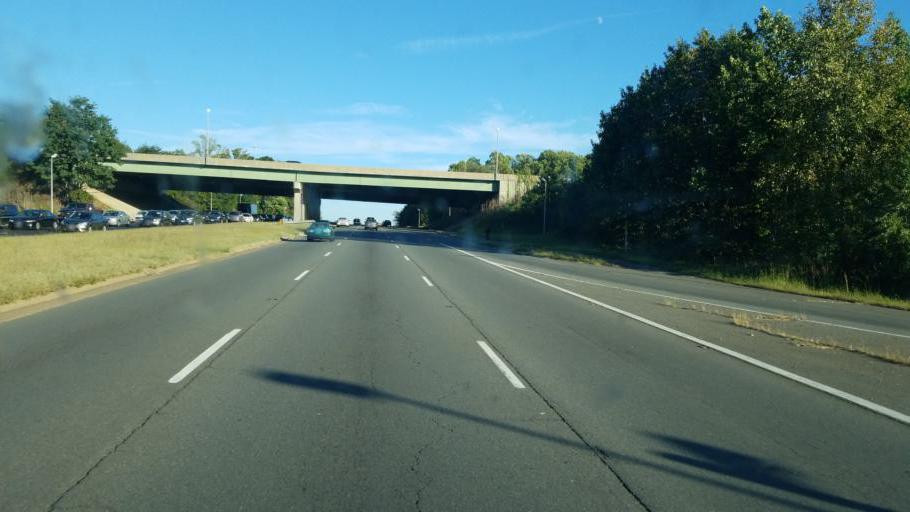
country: US
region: Virginia
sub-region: Fairfax County
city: Greenbriar
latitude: 38.8760
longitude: -77.3849
